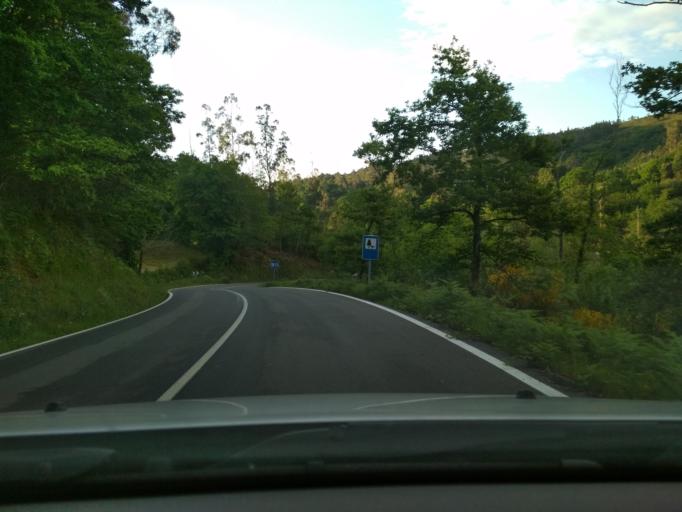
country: ES
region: Galicia
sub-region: Provincia da Coruna
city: Mazaricos
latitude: 42.9033
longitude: -8.9366
